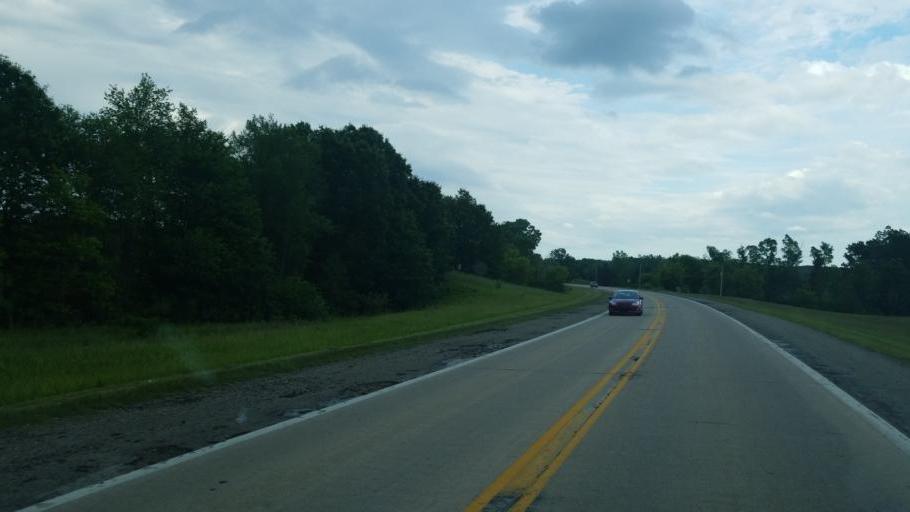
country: US
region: Michigan
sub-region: Eaton County
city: Bellevue
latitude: 42.4333
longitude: -85.0108
